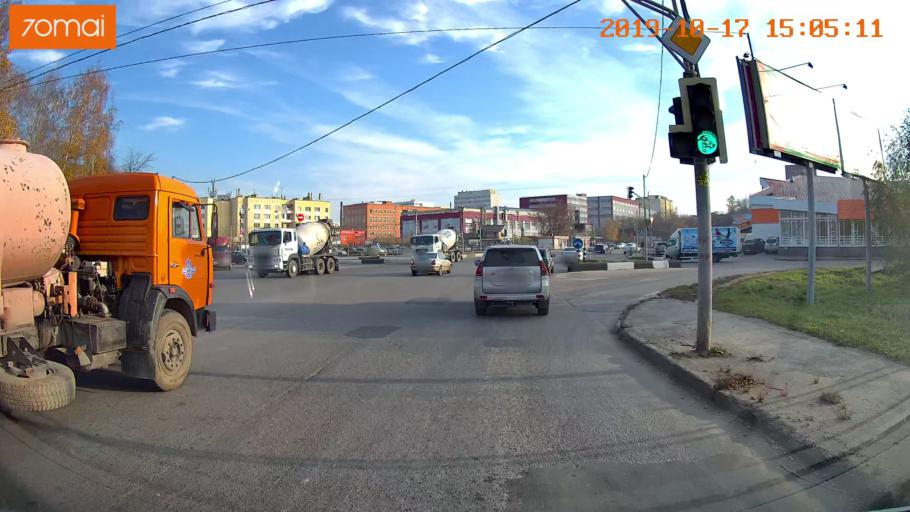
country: RU
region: Rjazan
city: Ryazan'
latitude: 54.6373
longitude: 39.7226
